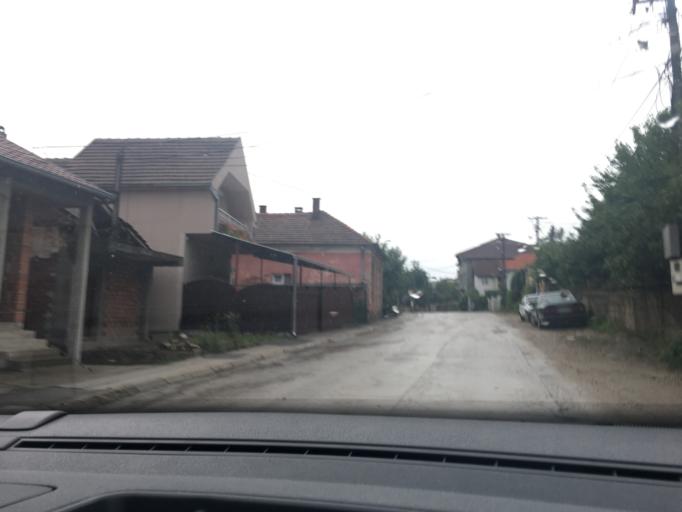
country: RS
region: Central Serbia
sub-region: Nisavski Okrug
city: Aleksinac
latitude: 43.5455
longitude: 21.7060
